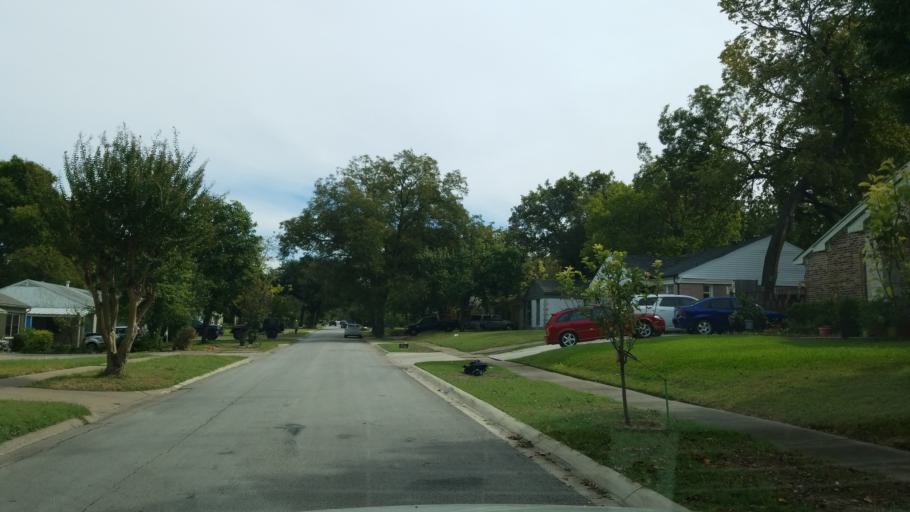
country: US
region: Texas
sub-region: Dallas County
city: Dallas
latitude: 32.7747
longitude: -96.7174
